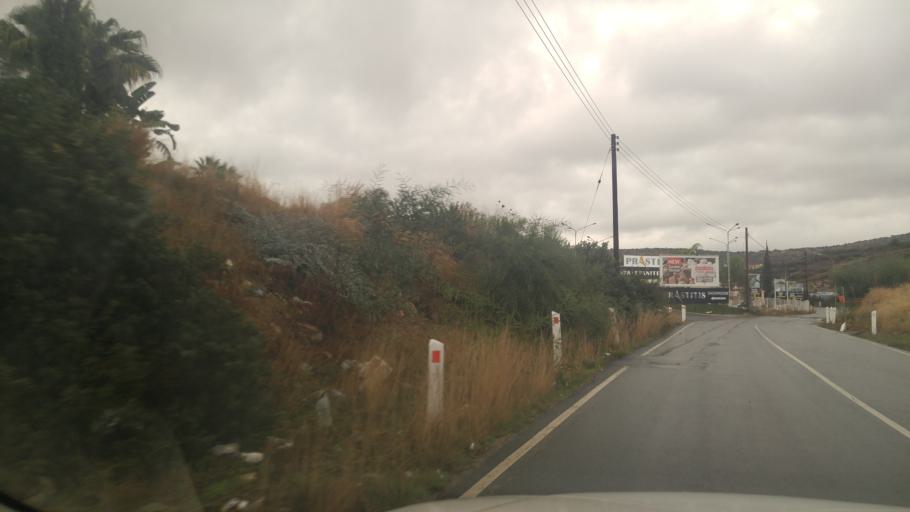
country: CY
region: Limassol
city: Mouttagiaka
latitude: 34.7088
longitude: 33.1091
